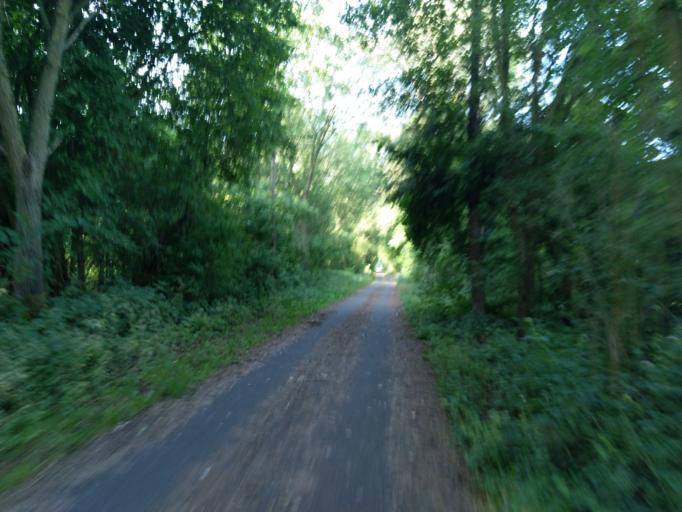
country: BE
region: Wallonia
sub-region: Province du Hainaut
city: Estinnes-au-Val
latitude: 50.3603
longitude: 4.1117
